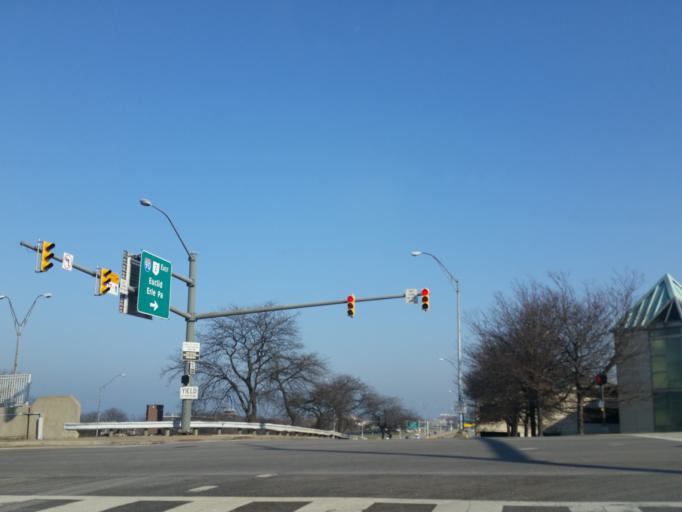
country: US
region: Ohio
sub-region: Cuyahoga County
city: Cleveland
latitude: 41.5074
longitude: -81.6934
